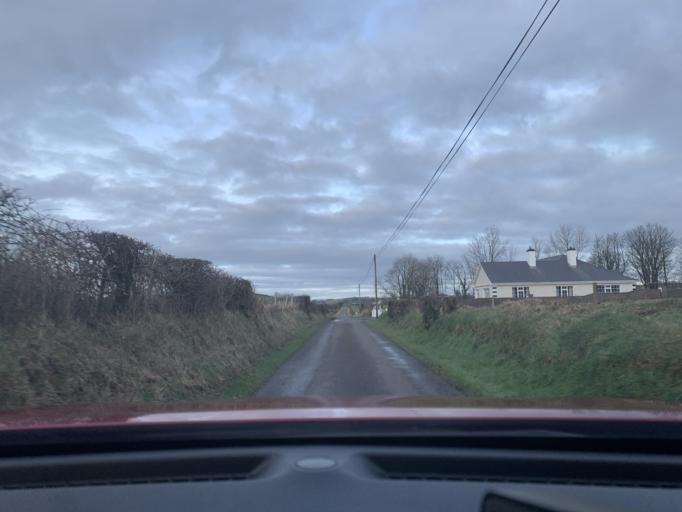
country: IE
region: Connaught
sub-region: Sligo
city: Ballymote
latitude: 54.0465
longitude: -8.5741
